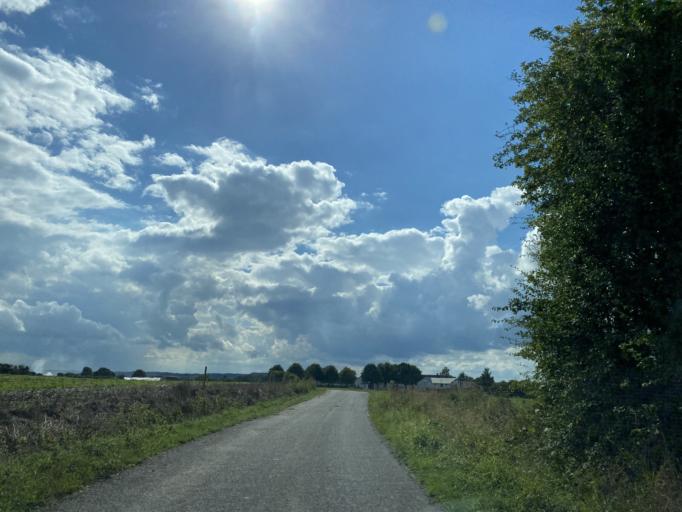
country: DK
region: South Denmark
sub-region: Haderslev Kommune
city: Starup
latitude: 55.1879
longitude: 9.5096
